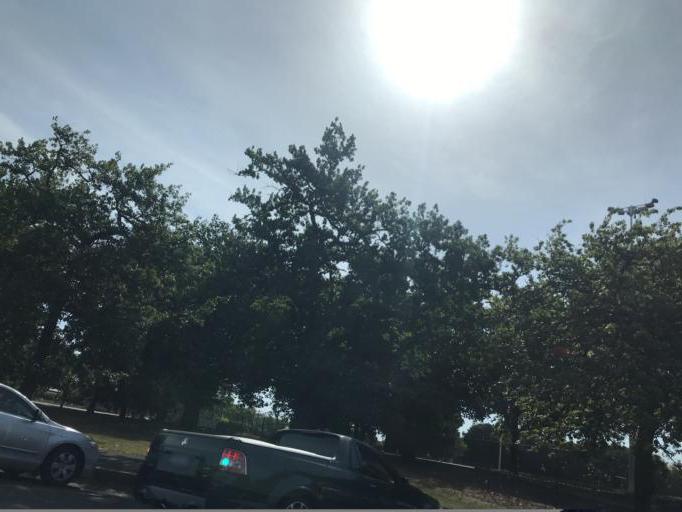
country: AU
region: Victoria
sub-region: Ballarat North
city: Lake Wendouree
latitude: -37.5587
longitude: 143.8392
